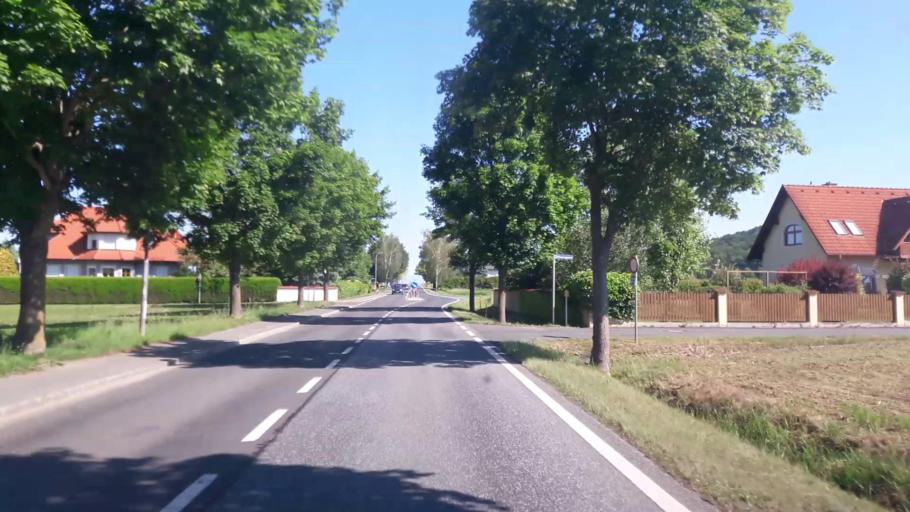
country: AT
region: Burgenland
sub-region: Politischer Bezirk Jennersdorf
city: Rudersdorf
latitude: 47.0558
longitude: 16.1184
